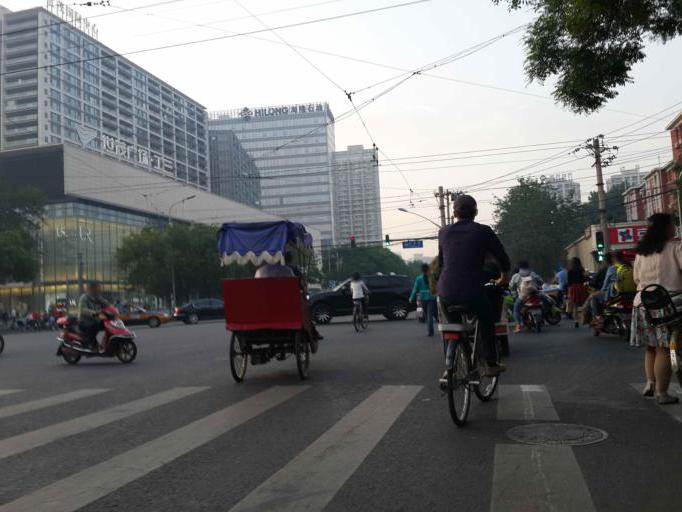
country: CN
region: Beijing
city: Chaowai
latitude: 39.9321
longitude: 116.4444
